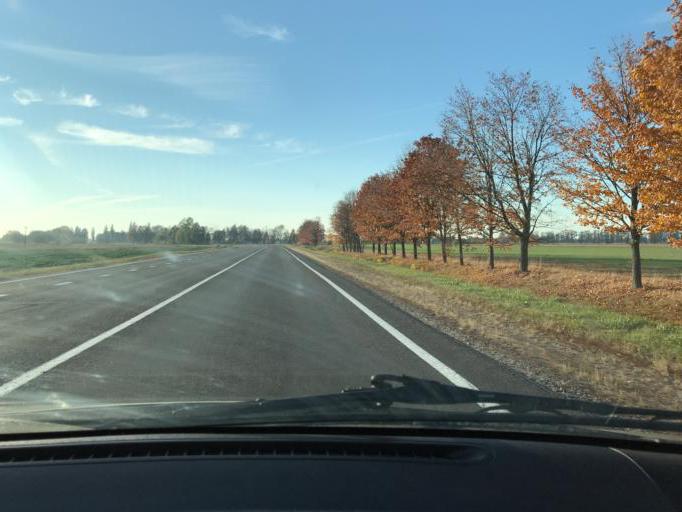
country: BY
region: Brest
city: Horad Kobryn
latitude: 52.2173
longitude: 24.5102
